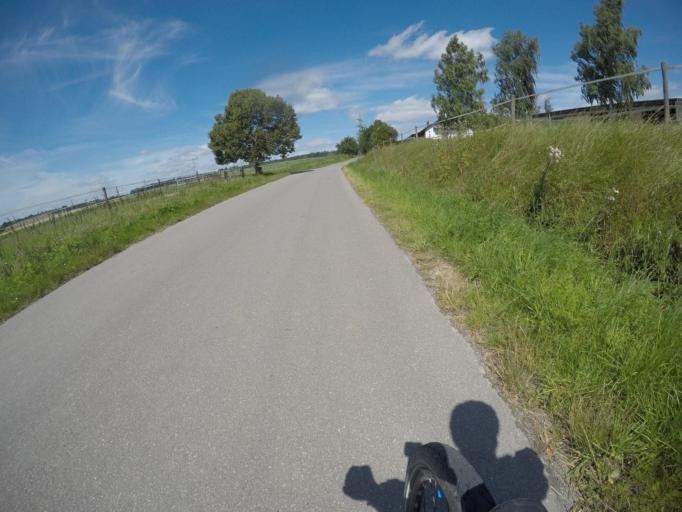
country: DE
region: Baden-Wuerttemberg
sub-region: Regierungsbezirk Stuttgart
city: Ehningen
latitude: 48.6591
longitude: 8.9229
